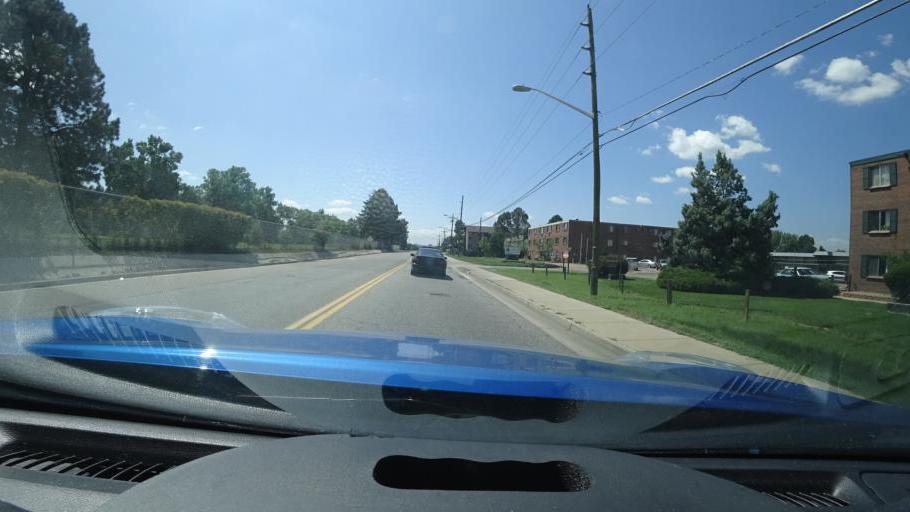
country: US
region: Colorado
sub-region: Arapahoe County
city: Glendale
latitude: 39.7022
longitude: -104.9035
